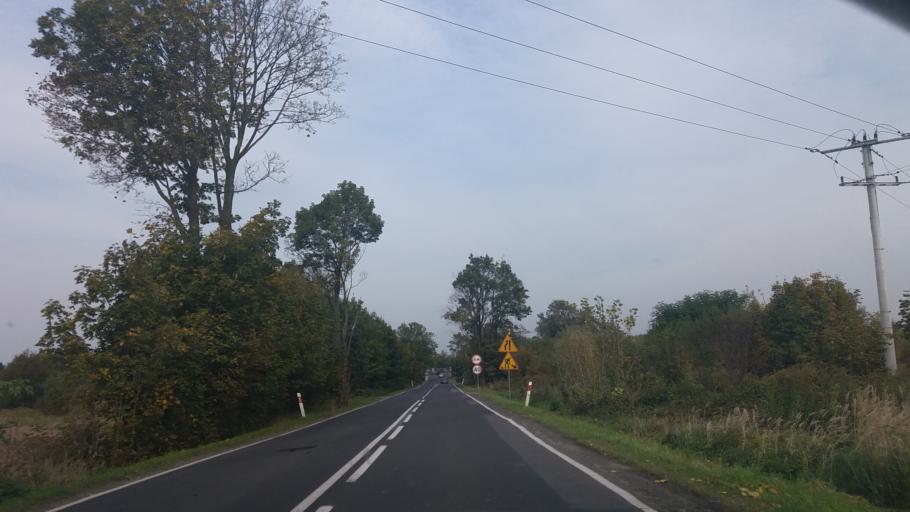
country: PL
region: Lesser Poland Voivodeship
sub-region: Powiat chrzanowski
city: Babice
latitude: 50.0363
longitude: 19.4391
